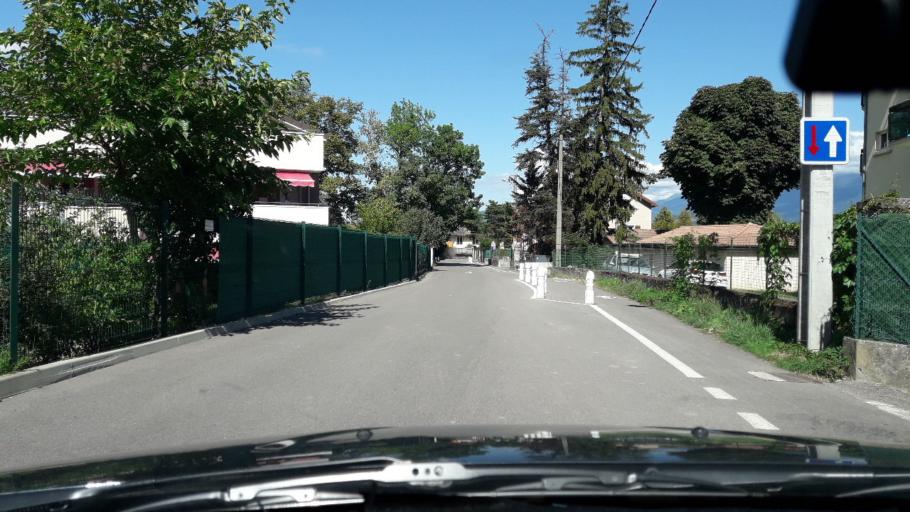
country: FR
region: Rhone-Alpes
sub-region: Departement de l'Isere
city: Vif
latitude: 45.0587
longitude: 5.6719
